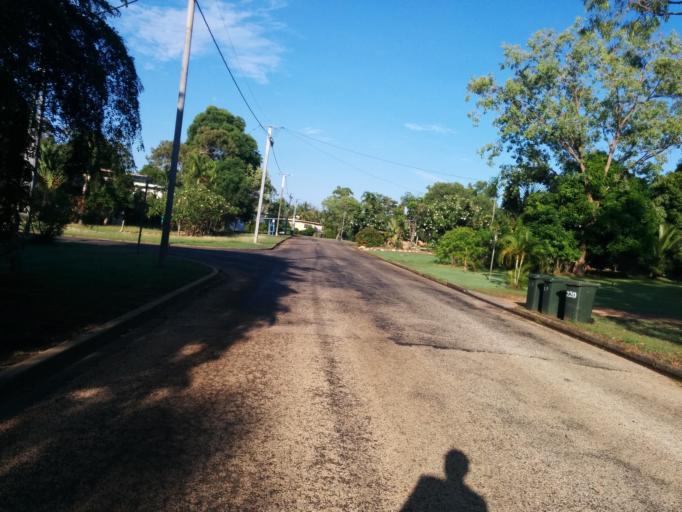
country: AU
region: Northern Territory
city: Alyangula
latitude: -13.8443
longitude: 136.4166
